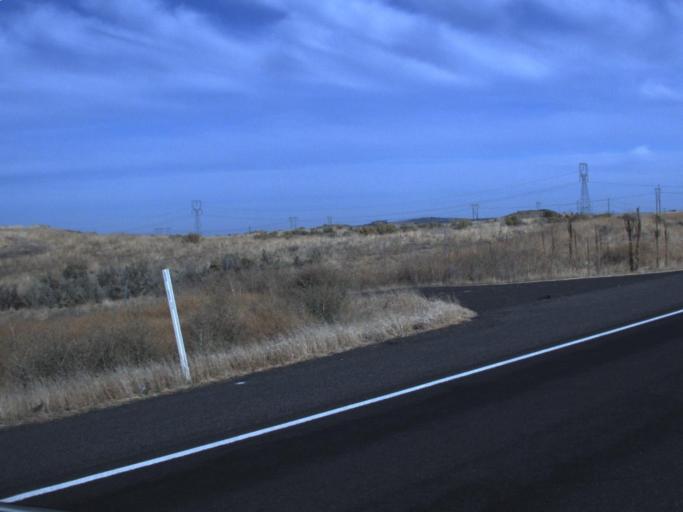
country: US
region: Washington
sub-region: Franklin County
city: Connell
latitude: 46.6366
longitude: -119.0063
